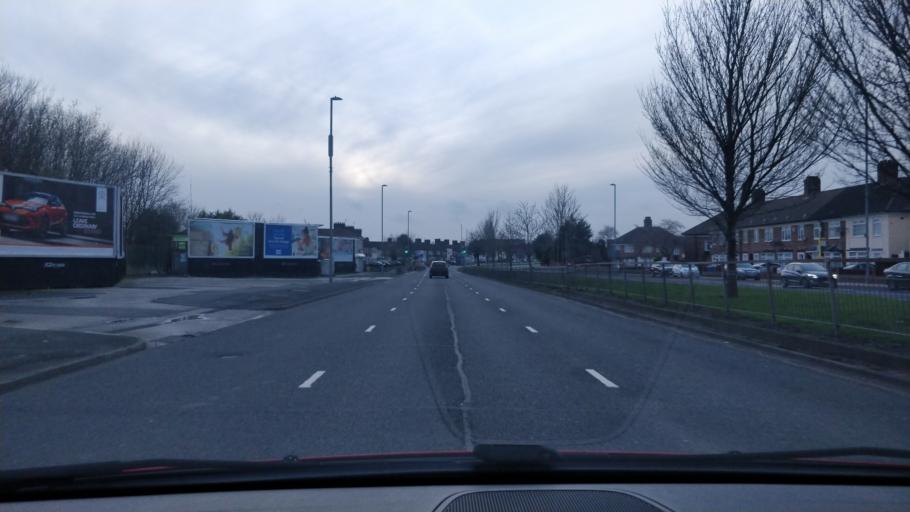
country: GB
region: England
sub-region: Knowsley
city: Huyton
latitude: 53.4209
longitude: -2.8656
